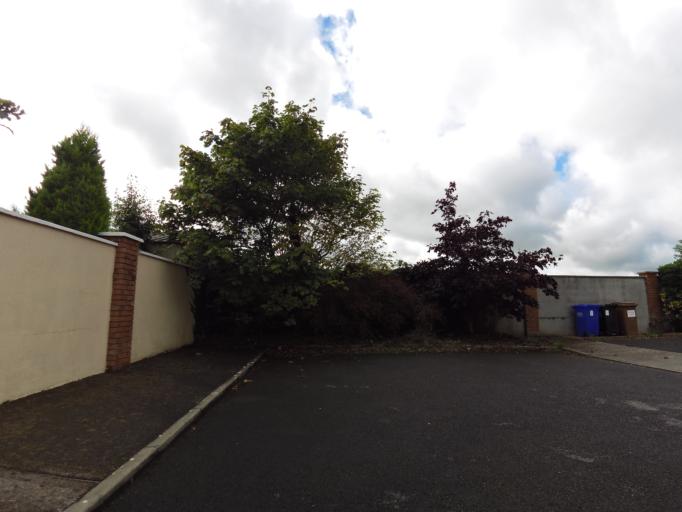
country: IE
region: Connaught
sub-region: County Galway
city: Loughrea
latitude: 53.2019
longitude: -8.5513
